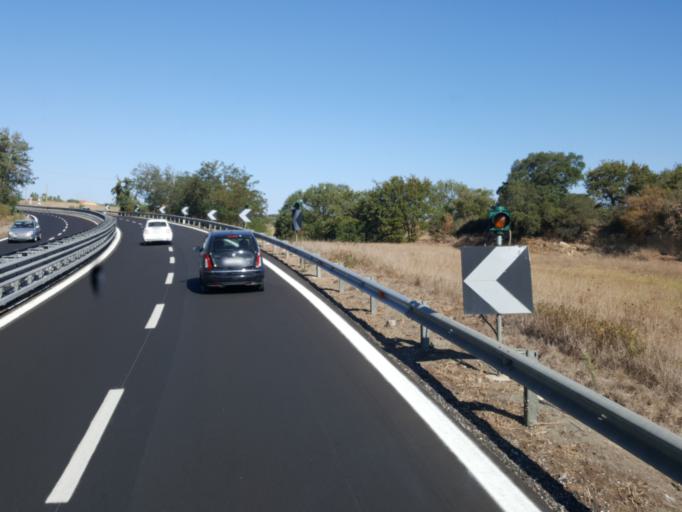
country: IT
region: Latium
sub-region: Provincia di Viterbo
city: Montalto di Castro
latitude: 42.3245
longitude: 11.6393
